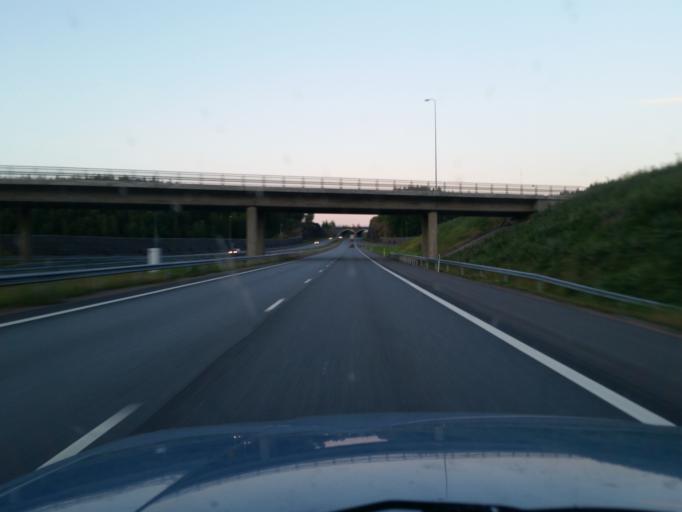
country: FI
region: Uusimaa
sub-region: Helsinki
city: Sammatti
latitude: 60.3782
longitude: 23.8037
